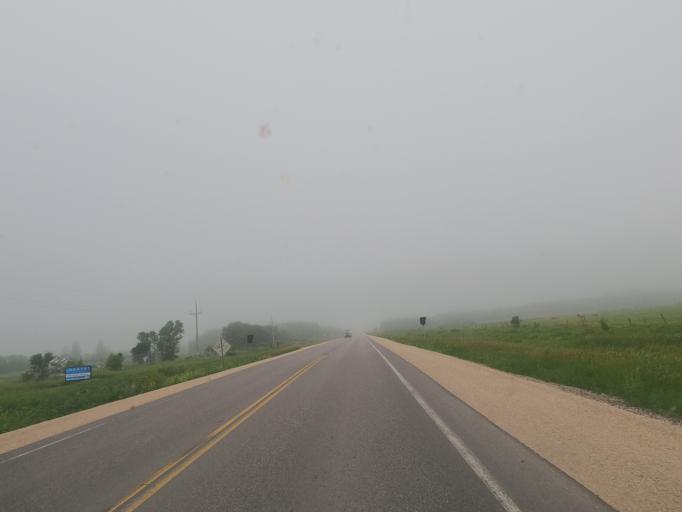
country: CA
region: Manitoba
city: Carman
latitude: 49.6801
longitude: -98.0094
